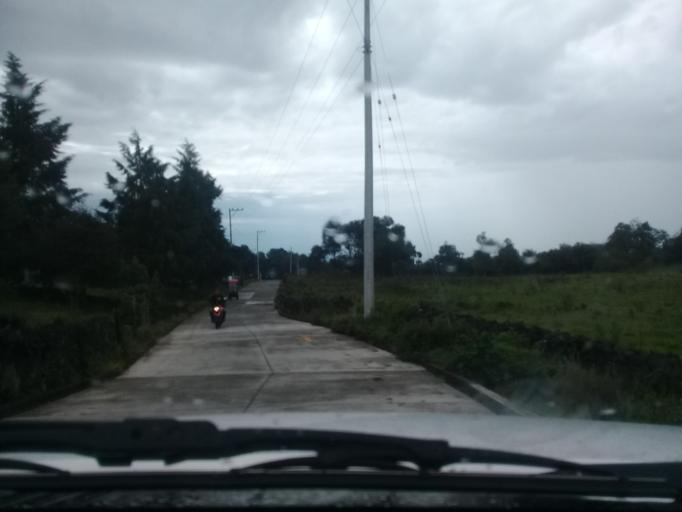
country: MX
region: Veracruz
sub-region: Acajete
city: La Joya
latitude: 19.6163
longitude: -97.0042
